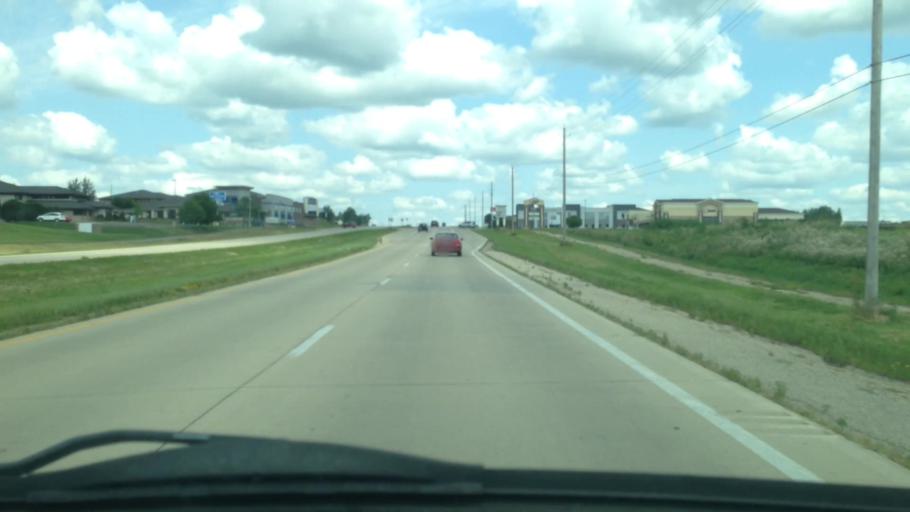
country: US
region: Minnesota
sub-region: Olmsted County
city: Rochester
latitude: 44.0487
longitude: -92.5213
